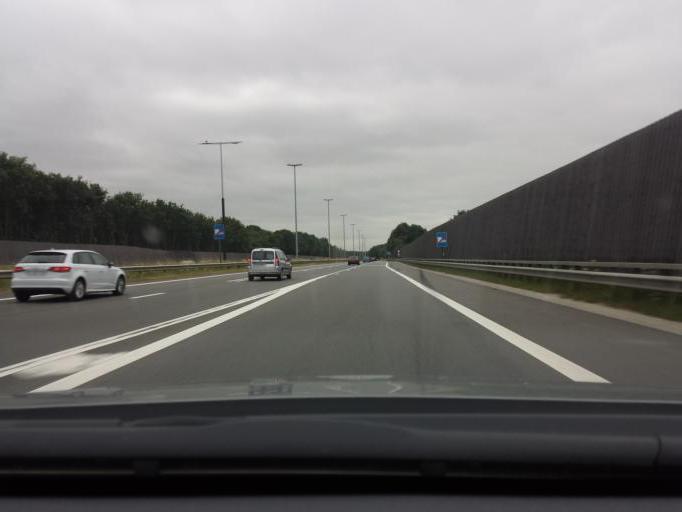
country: BE
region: Flanders
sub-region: Provincie Limburg
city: Lummen
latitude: 50.9983
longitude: 5.2112
